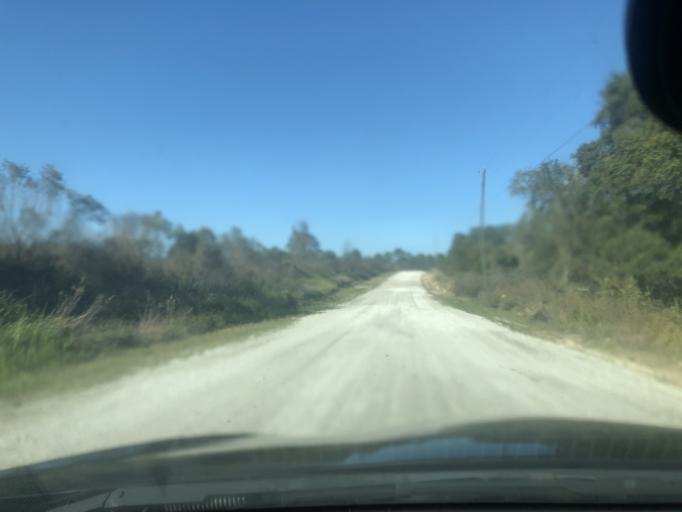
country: US
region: Florida
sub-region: Citrus County
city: Lecanto
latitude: 28.8235
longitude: -82.5180
